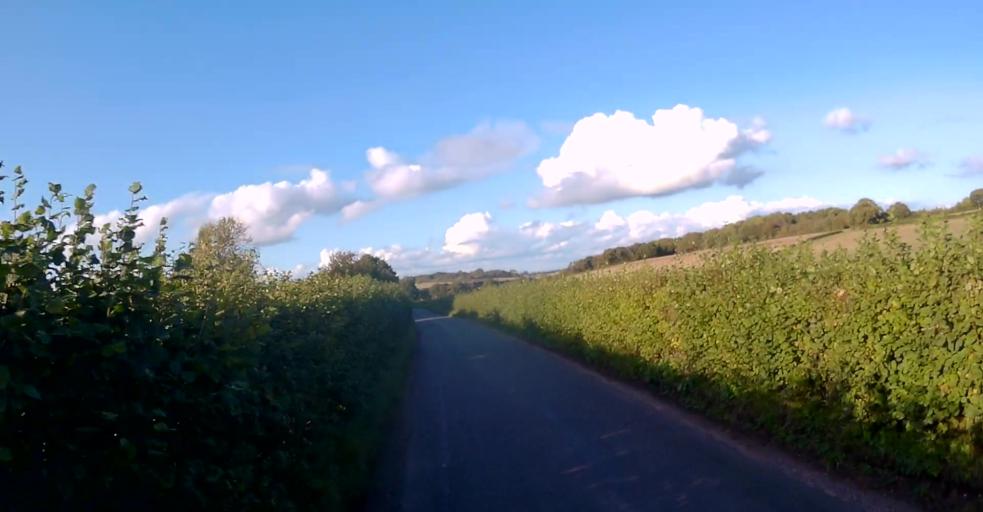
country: GB
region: England
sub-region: Hampshire
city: Long Sutton
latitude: 51.2276
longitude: -0.9241
